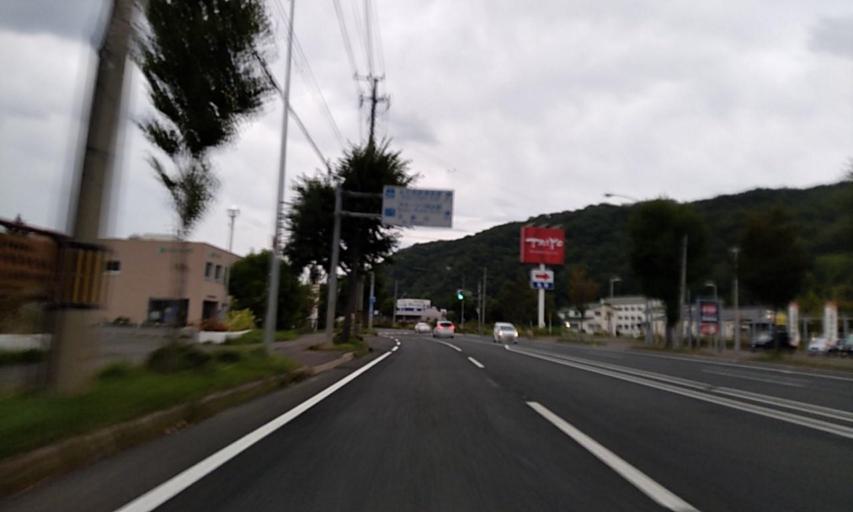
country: JP
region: Hokkaido
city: Abashiri
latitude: 44.0143
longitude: 144.2378
